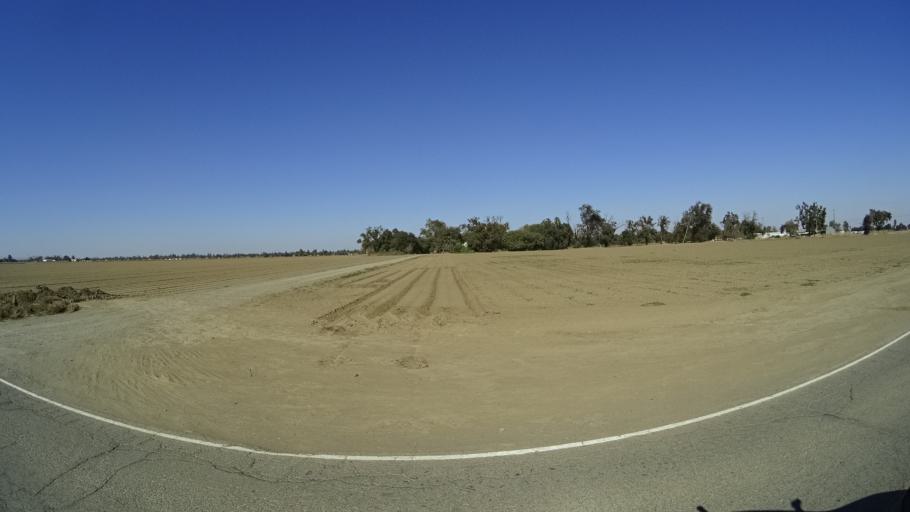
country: US
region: California
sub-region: Yolo County
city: Woodland
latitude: 38.6410
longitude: -121.7687
